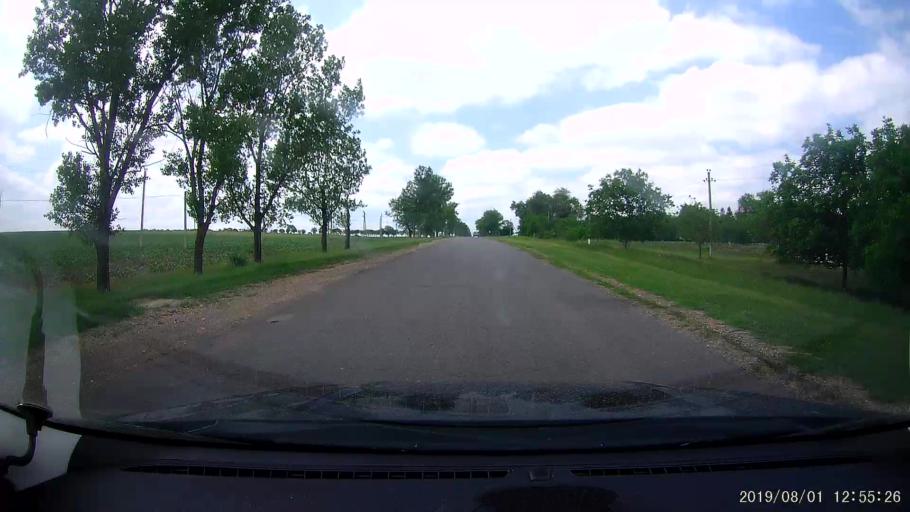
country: MD
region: Gagauzia
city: Vulcanesti
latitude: 45.6939
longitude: 28.4670
